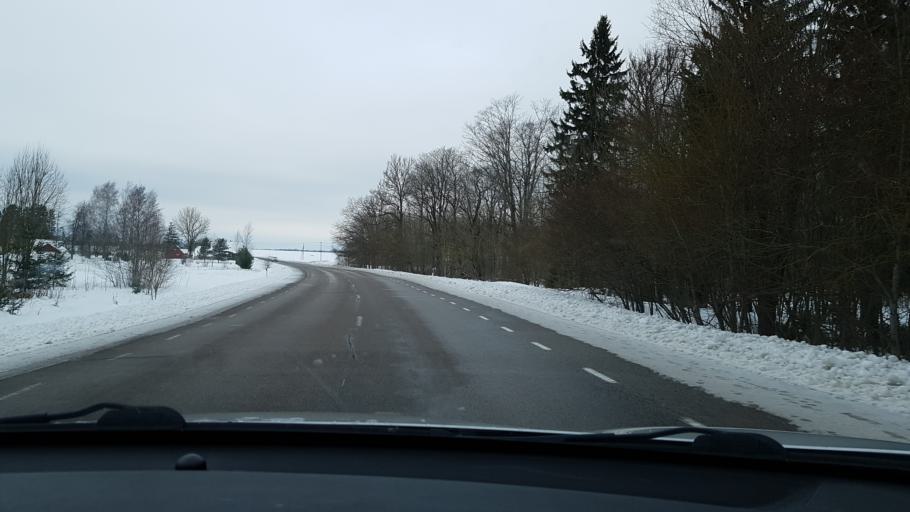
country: EE
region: Jaervamaa
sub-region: Paide linn
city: Paide
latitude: 58.8978
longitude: 25.7459
